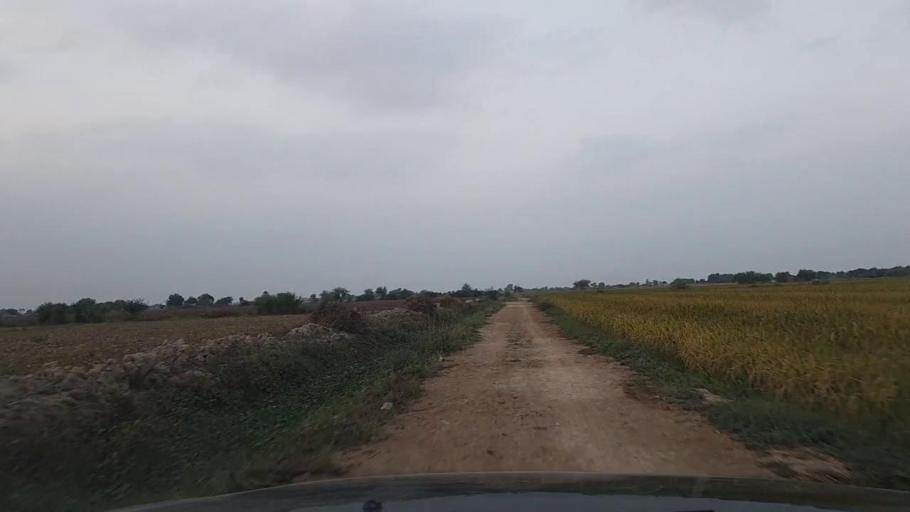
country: PK
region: Sindh
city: Jati
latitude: 24.5070
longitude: 68.3931
